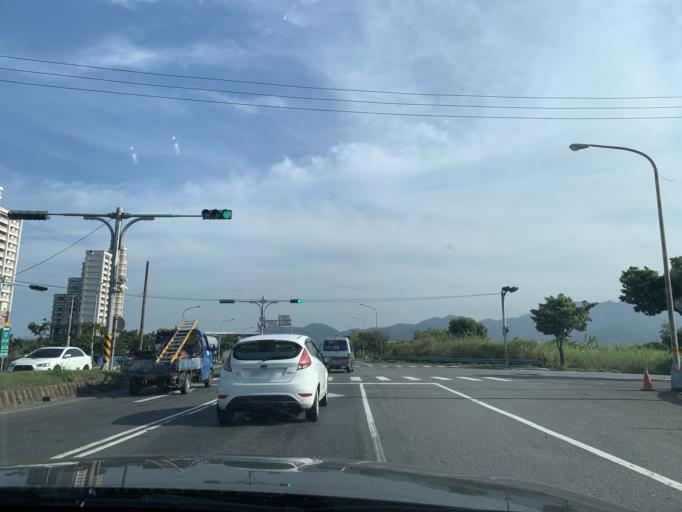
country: TW
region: Taiwan
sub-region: Yilan
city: Yilan
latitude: 24.6691
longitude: 121.8276
